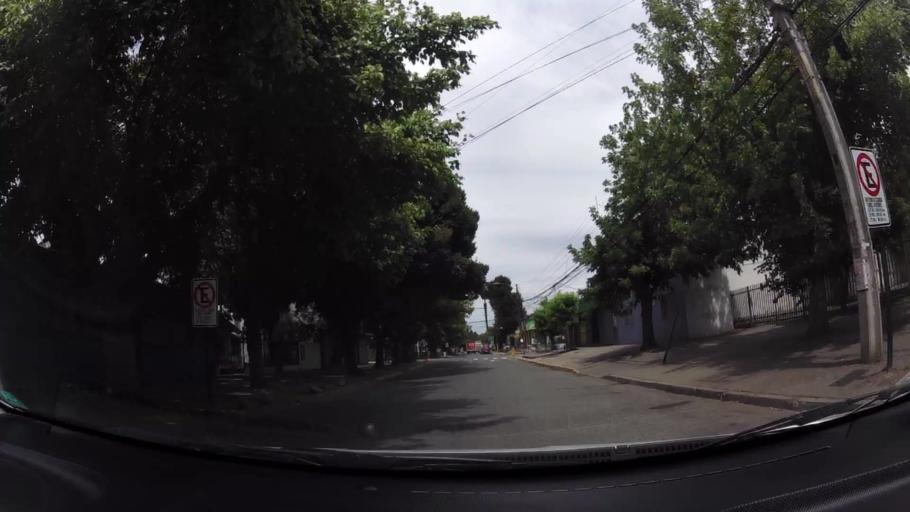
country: CL
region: O'Higgins
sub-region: Provincia de Cachapoal
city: Graneros
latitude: -34.0657
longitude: -70.7275
